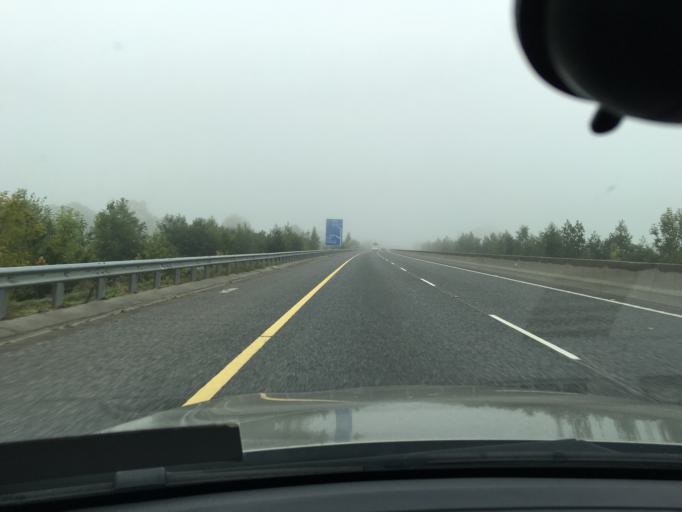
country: IE
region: Leinster
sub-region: An Iarmhi
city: Moate
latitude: 53.3885
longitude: -7.7551
